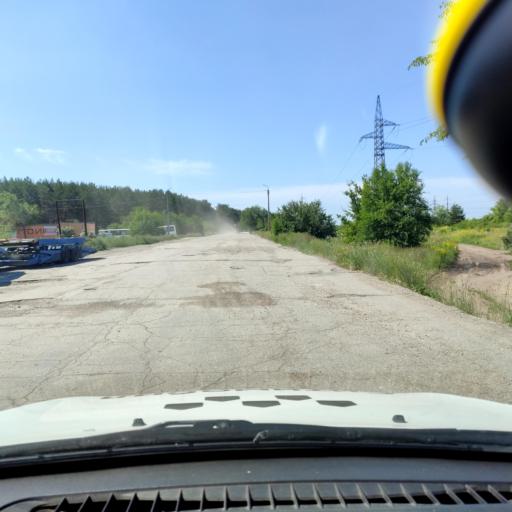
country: RU
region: Samara
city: Zhigulevsk
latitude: 53.5408
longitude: 49.5128
